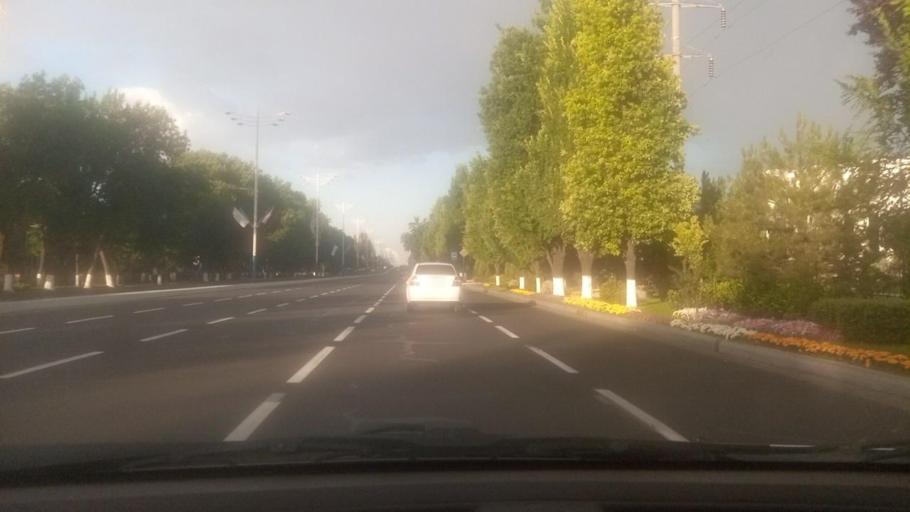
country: UZ
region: Toshkent
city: Salor
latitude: 41.3375
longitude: 69.3380
